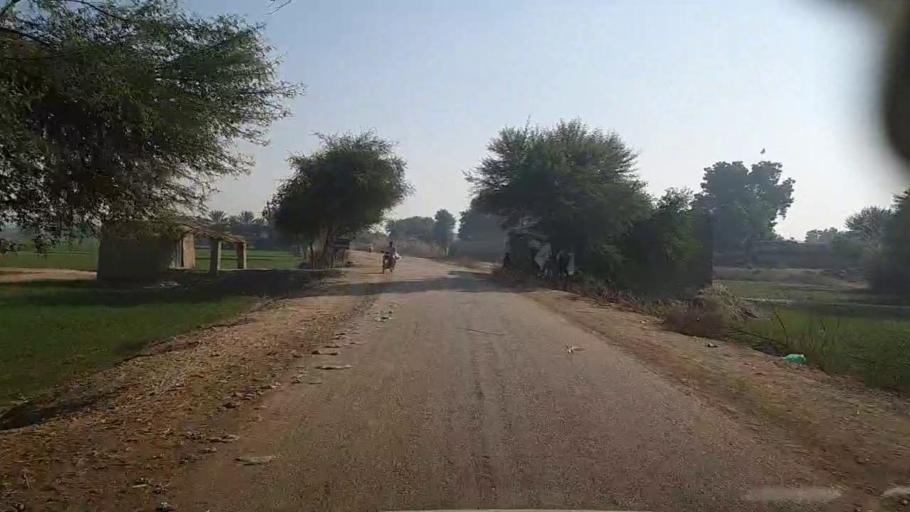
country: PK
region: Sindh
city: Kandiari
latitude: 26.8158
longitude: 68.4954
